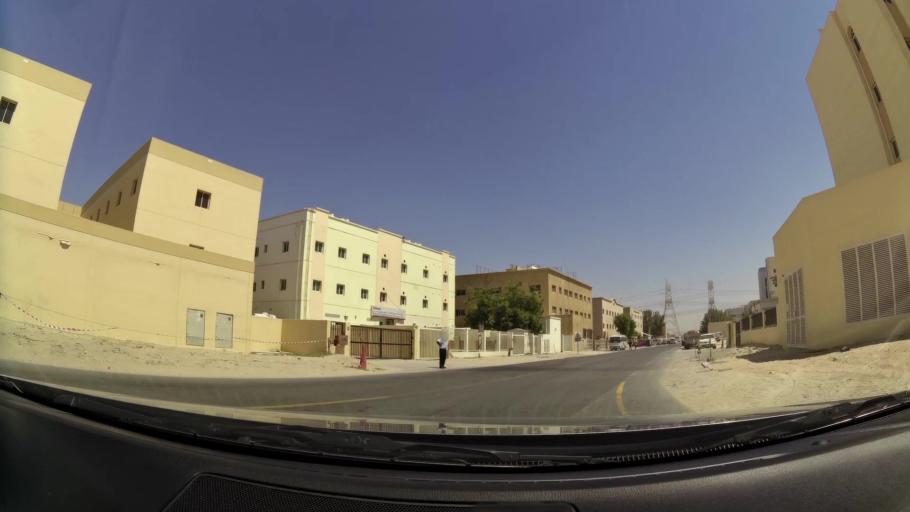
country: AE
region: Dubai
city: Dubai
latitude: 24.9881
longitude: 55.1987
